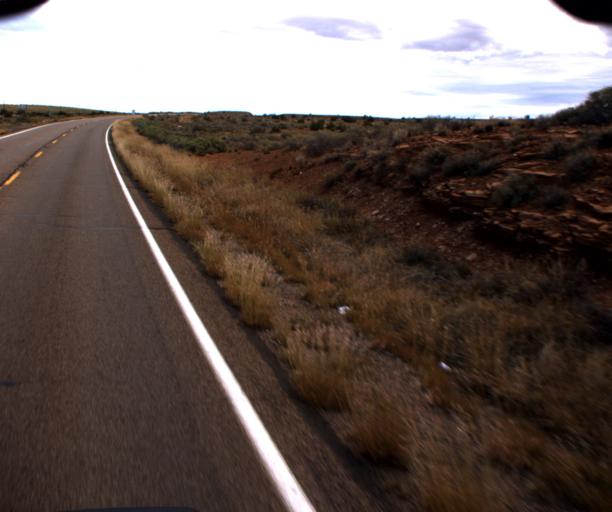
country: US
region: Arizona
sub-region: Navajo County
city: Holbrook
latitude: 34.8543
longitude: -110.1501
